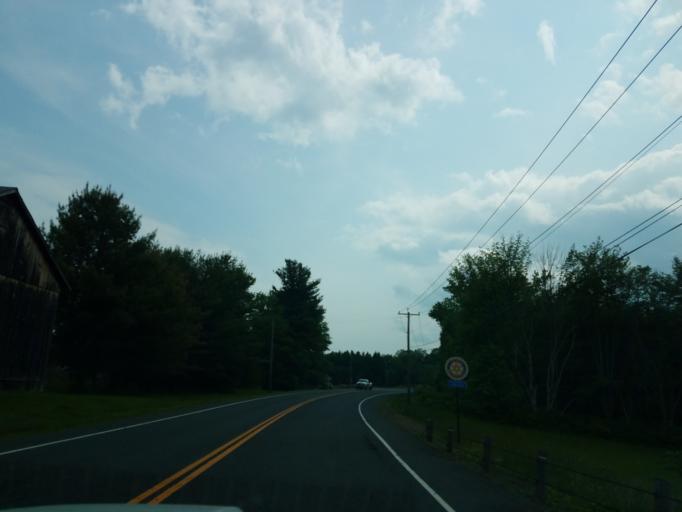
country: US
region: Massachusetts
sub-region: Hampden County
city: Agawam
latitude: 42.0290
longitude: -72.6371
